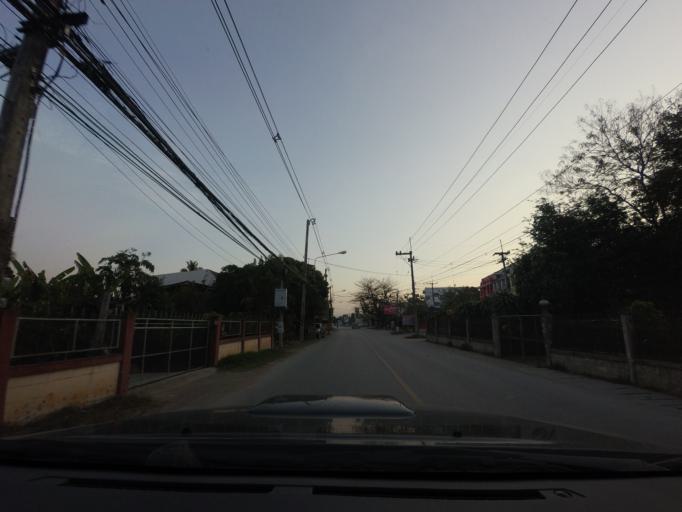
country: TH
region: Chiang Mai
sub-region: Amphoe Chiang Dao
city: Chiang Dao
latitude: 19.3636
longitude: 98.9645
